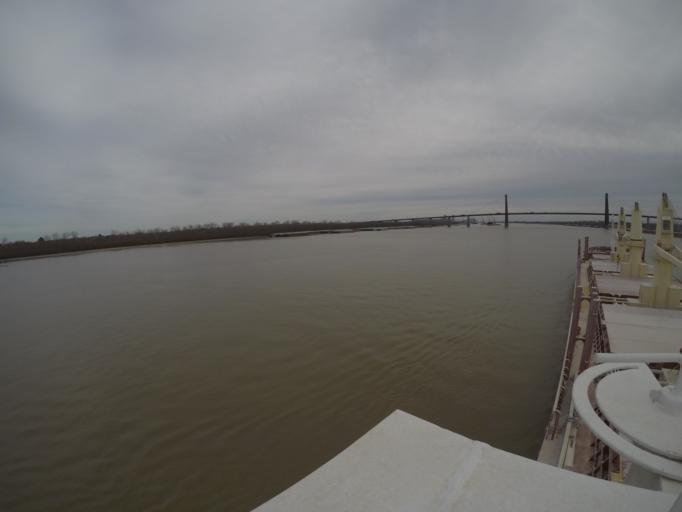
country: US
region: Louisiana
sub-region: Saint Charles Parish
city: Luling
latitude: 29.9464
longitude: -90.3855
